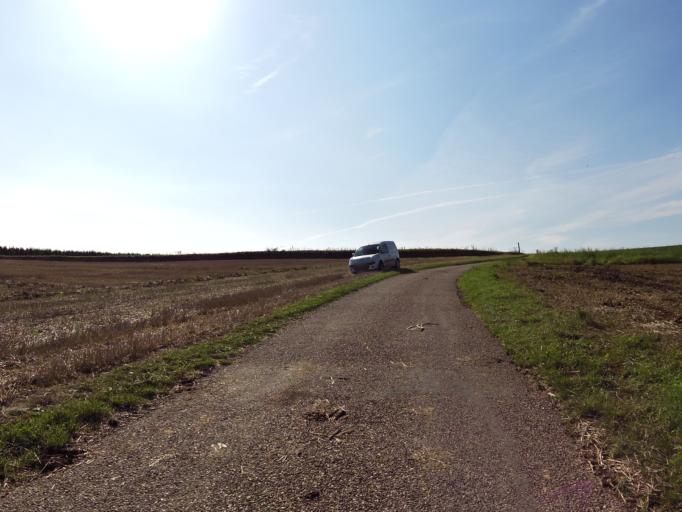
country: NL
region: Limburg
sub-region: Gemeente Voerendaal
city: Klimmen
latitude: 50.8544
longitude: 5.9052
